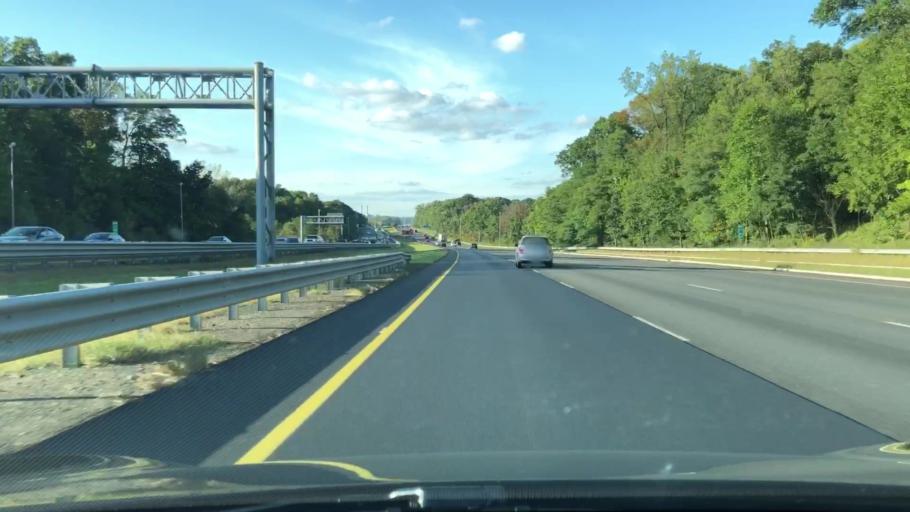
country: US
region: New Jersey
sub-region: Burlington County
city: Bordentown
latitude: 40.1373
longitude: -74.7159
